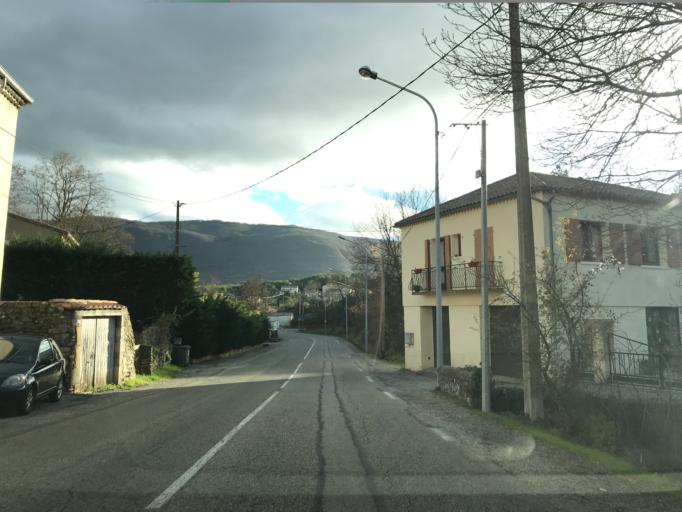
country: FR
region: Rhone-Alpes
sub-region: Departement de l'Ardeche
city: Privas
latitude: 44.7285
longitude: 4.5818
